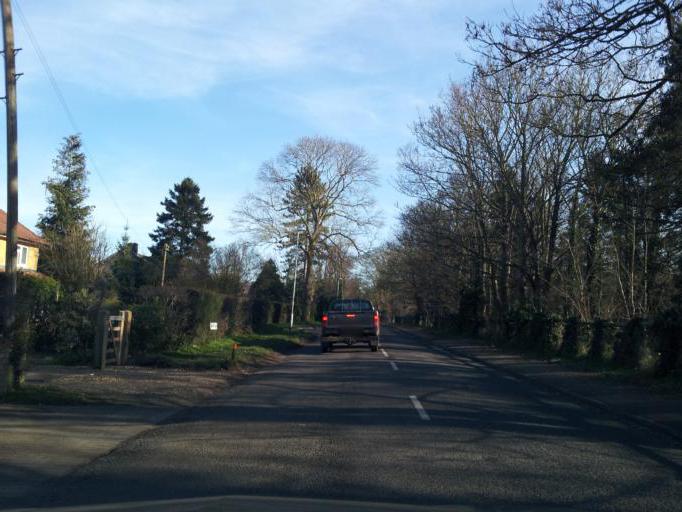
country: GB
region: England
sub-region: Cambridgeshire
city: Meldreth
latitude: 52.1116
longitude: 0.0358
